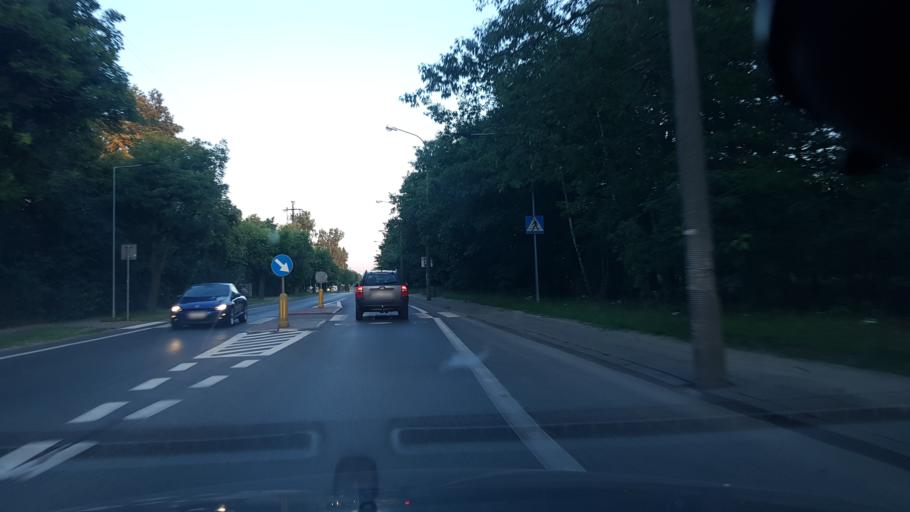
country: PL
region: Masovian Voivodeship
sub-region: Warszawa
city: Wawer
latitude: 52.1888
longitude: 21.1846
